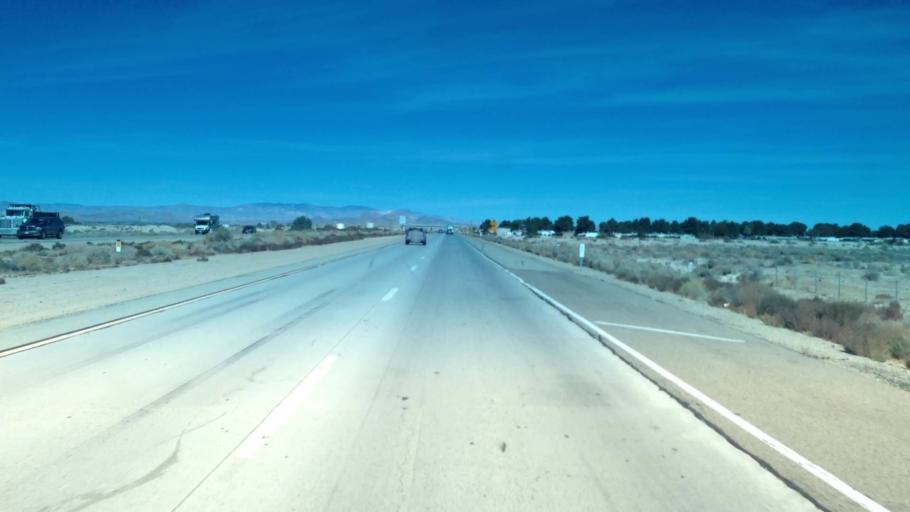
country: US
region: California
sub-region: Los Angeles County
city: Lancaster
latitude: 34.7527
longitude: -118.1703
